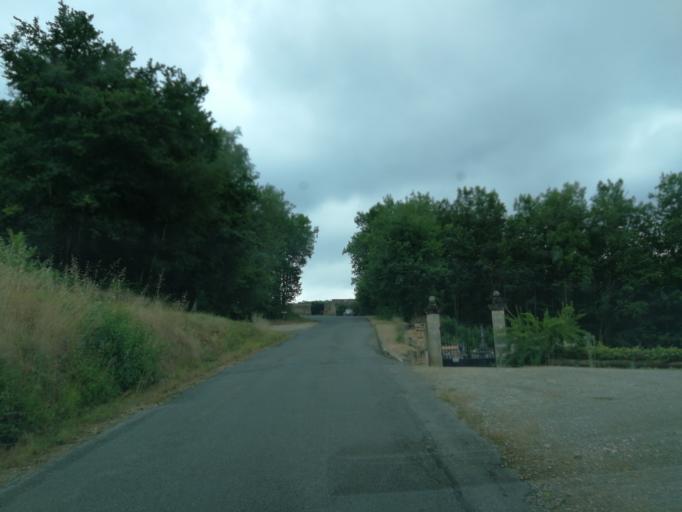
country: FR
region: Aquitaine
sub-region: Departement du Lot-et-Garonne
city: Montayral
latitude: 44.5409
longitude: 1.0767
